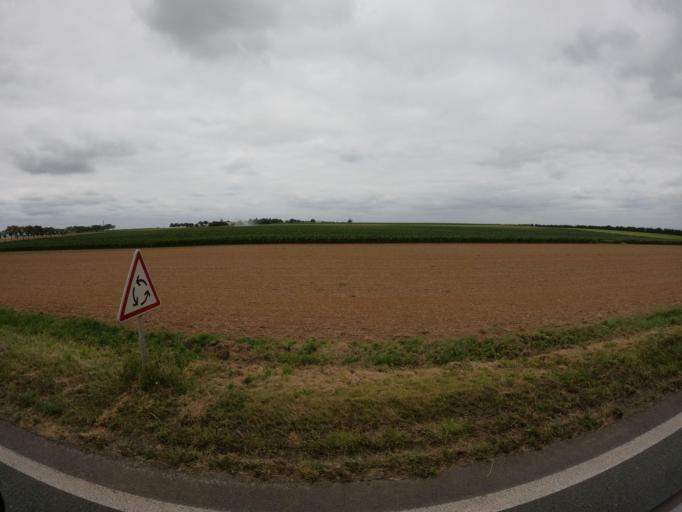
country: FR
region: Pays de la Loire
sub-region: Departement de la Vendee
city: Serigne
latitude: 46.4895
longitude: -0.9033
